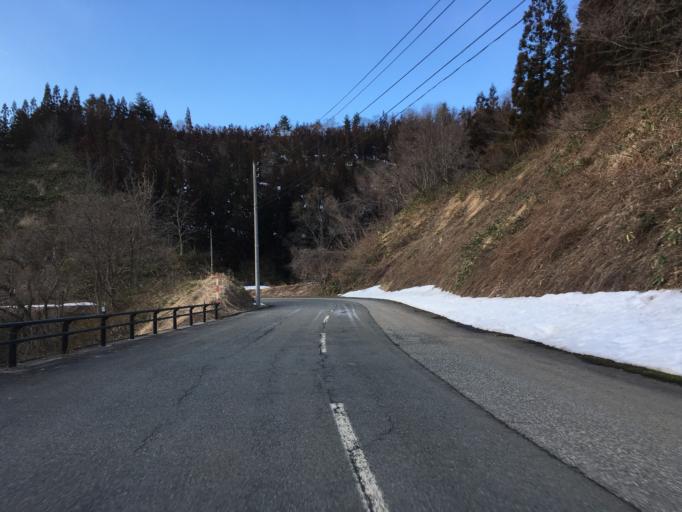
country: JP
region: Yamagata
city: Yonezawa
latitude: 37.9230
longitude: 139.9234
